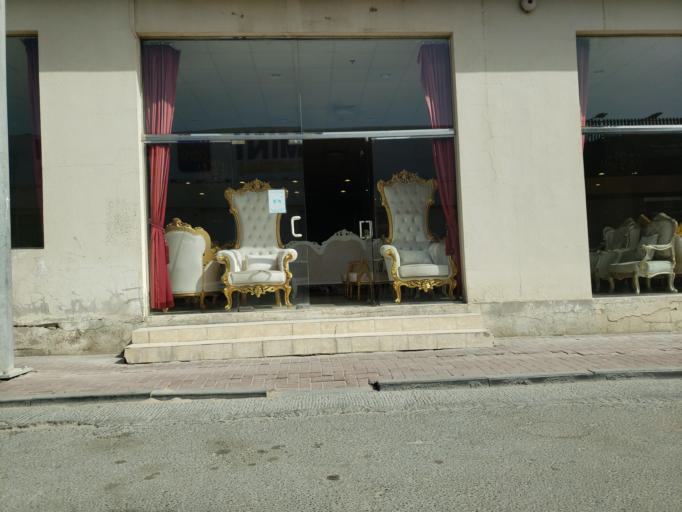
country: AE
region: Ash Shariqah
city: Sharjah
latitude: 25.3314
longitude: 55.4036
